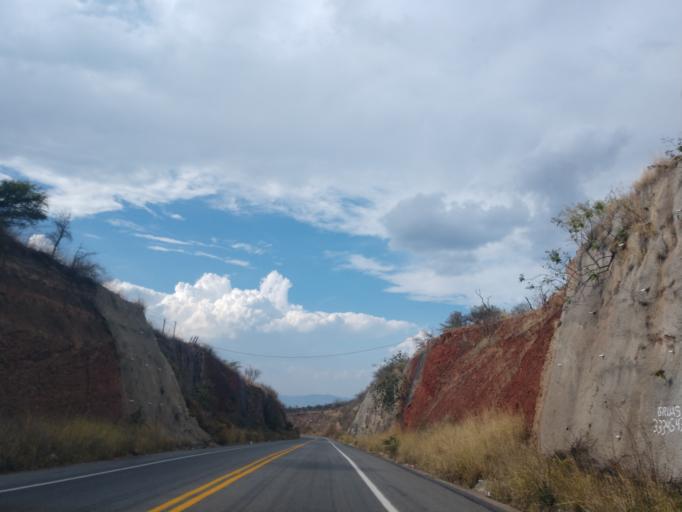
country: MX
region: Jalisco
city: La Manzanilla de la Paz
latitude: 20.0967
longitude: -103.1690
